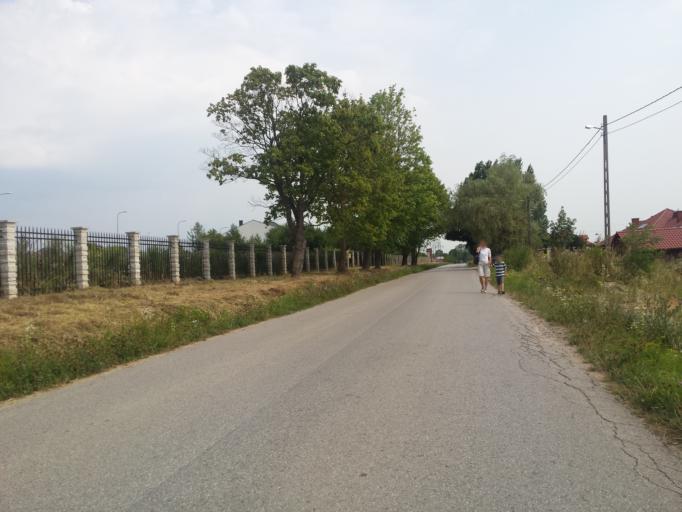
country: PL
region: Swietokrzyskie
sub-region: Powiat kielecki
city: Kielce
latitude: 50.8164
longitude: 20.6477
